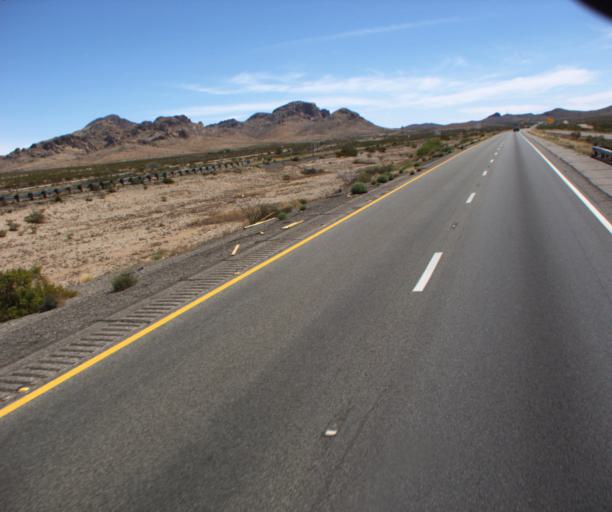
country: US
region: New Mexico
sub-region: Hidalgo County
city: Lordsburg
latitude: 32.2289
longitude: -109.0550
